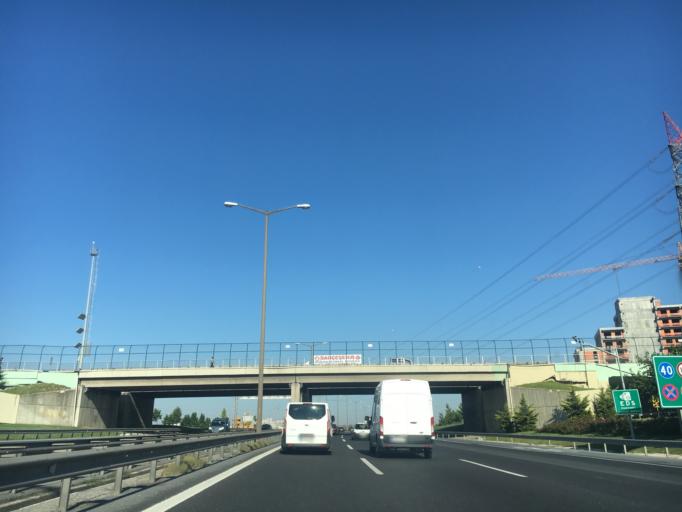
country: TR
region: Istanbul
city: Esenyurt
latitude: 41.0540
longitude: 28.6716
